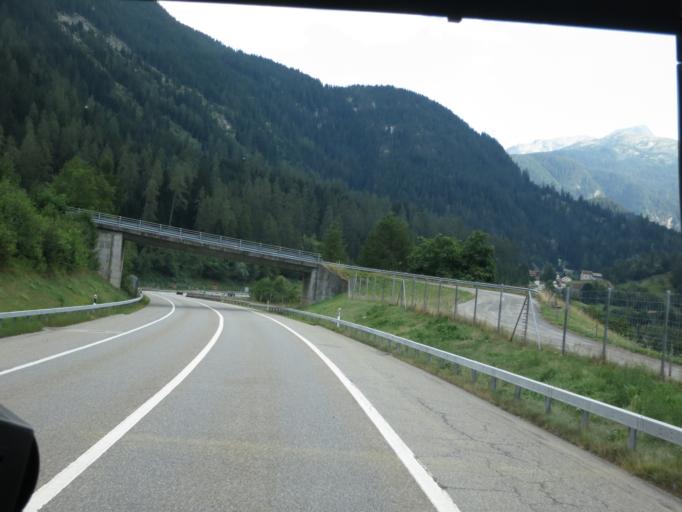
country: CH
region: Grisons
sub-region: Hinterrhein District
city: Thusis
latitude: 46.6026
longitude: 9.4302
